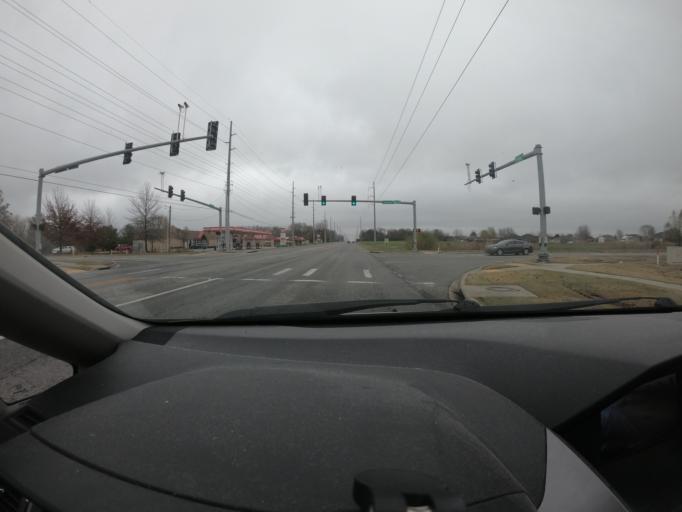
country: US
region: Arkansas
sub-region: Benton County
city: Bentonville
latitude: 36.3575
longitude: -94.2405
